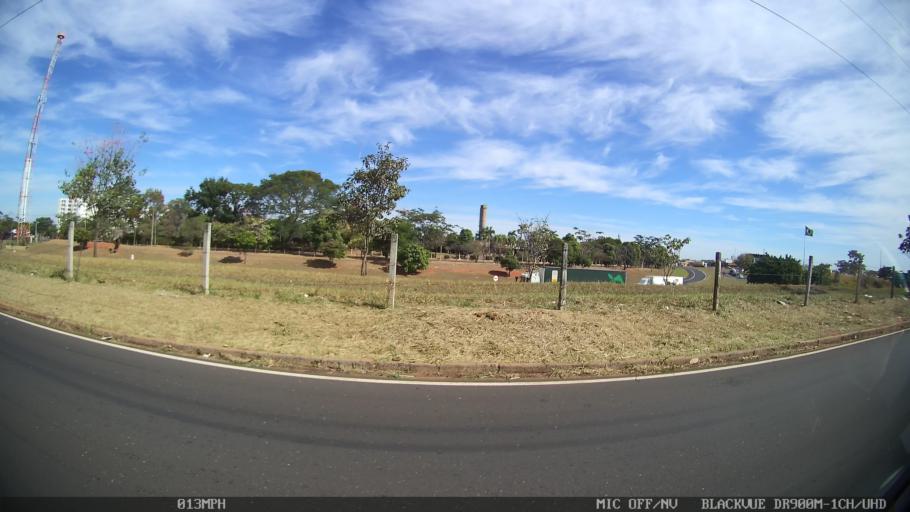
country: BR
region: Sao Paulo
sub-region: Sao Jose Do Rio Preto
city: Sao Jose do Rio Preto
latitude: -20.8319
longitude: -49.3600
